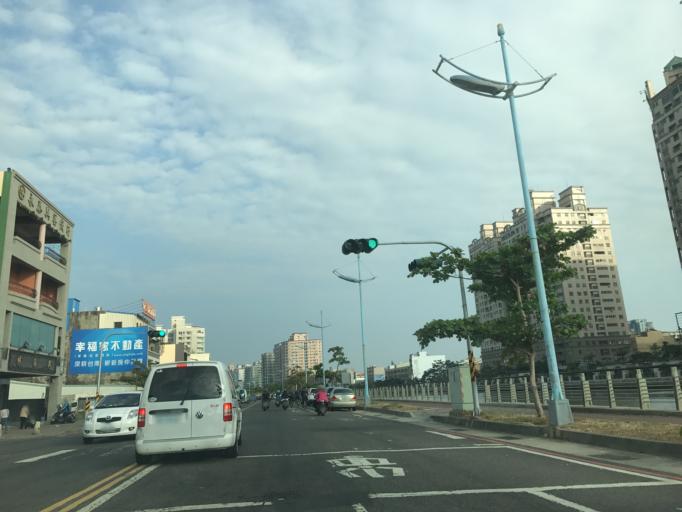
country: TW
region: Taiwan
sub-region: Tainan
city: Tainan
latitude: 22.9985
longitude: 120.1705
